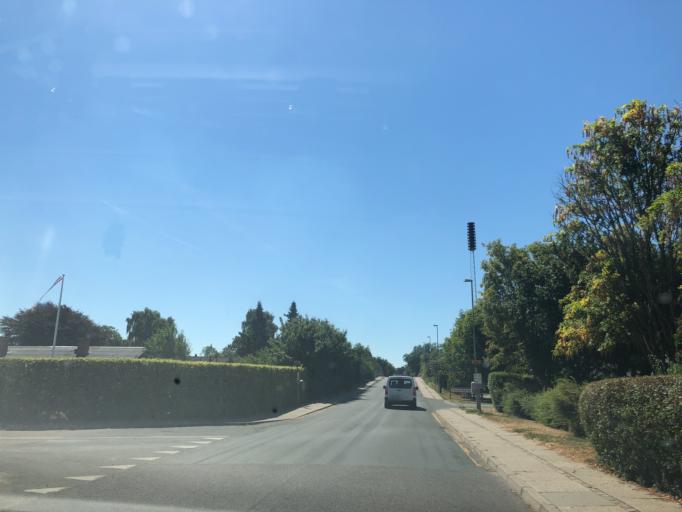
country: DK
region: Zealand
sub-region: Slagelse Kommune
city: Forlev
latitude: 55.3668
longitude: 11.2596
